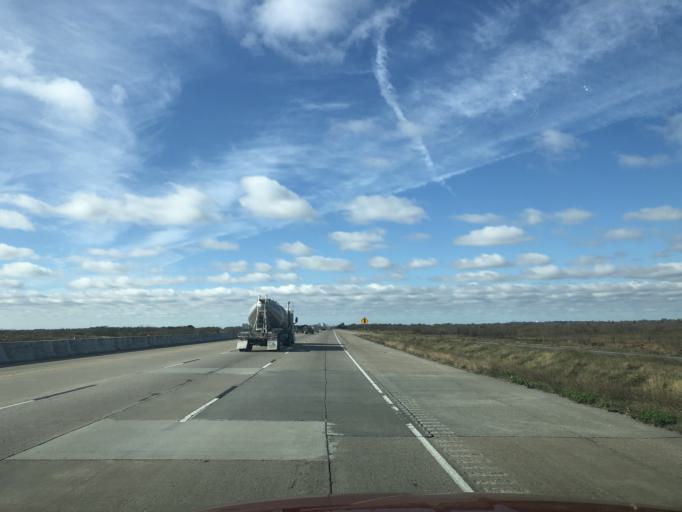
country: US
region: Texas
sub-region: Chambers County
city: Old River-Winfree
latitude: 29.8359
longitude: -94.7723
